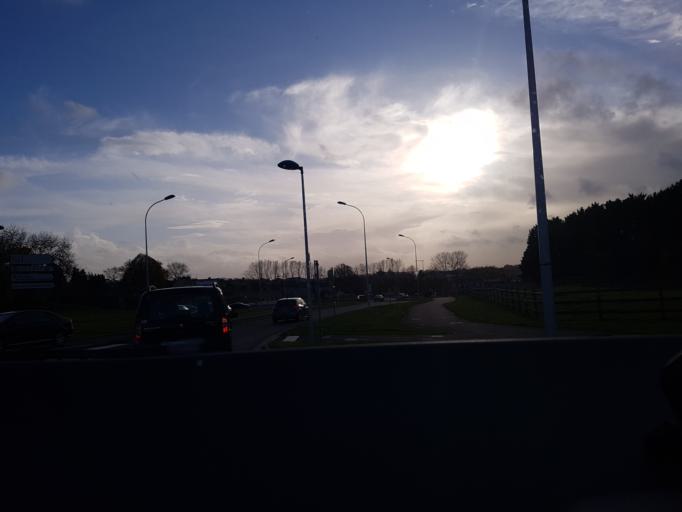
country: FR
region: Lower Normandy
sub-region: Departement du Calvados
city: Saint-Vigor-le-Grand
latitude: 49.2733
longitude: -0.6894
